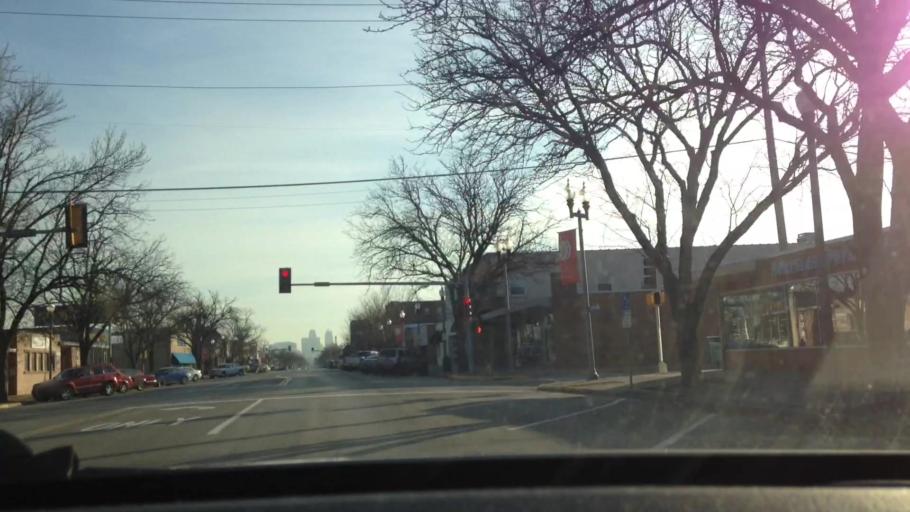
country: US
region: Missouri
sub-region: Clay County
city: North Kansas City
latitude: 39.1442
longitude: -94.5773
